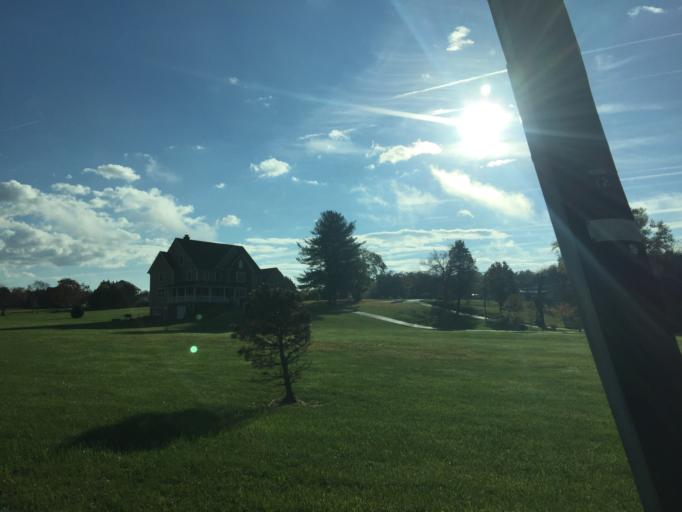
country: US
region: Maryland
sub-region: Howard County
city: Highland
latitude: 39.2675
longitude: -77.0121
